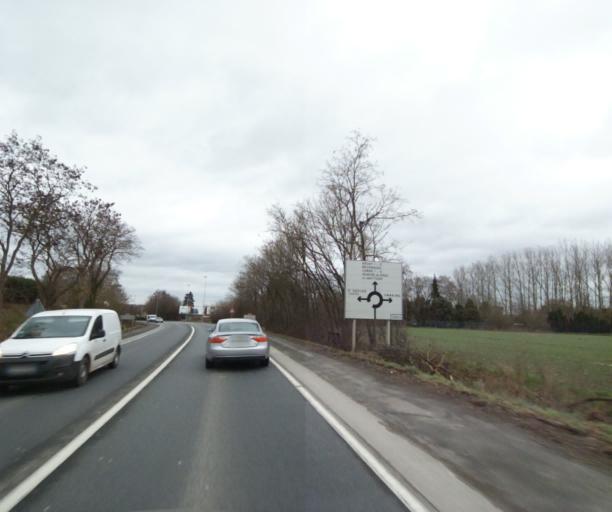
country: FR
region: Nord-Pas-de-Calais
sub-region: Departement du Nord
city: Saint-Saulve
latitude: 50.3736
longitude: 3.5700
